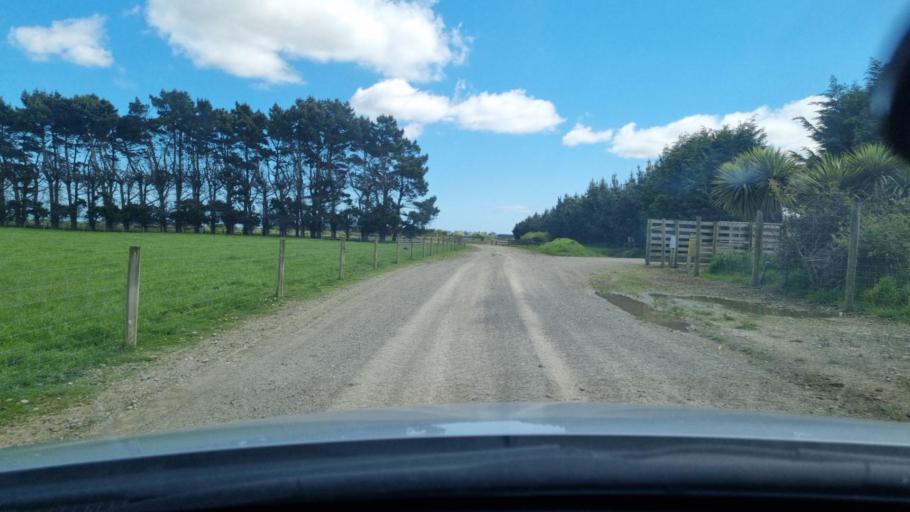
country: NZ
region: Southland
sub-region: Invercargill City
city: Invercargill
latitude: -46.3510
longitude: 168.2998
